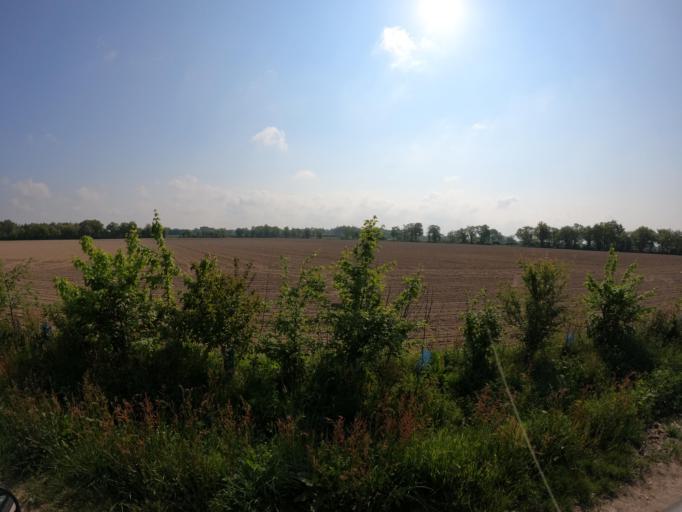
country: FR
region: Pays de la Loire
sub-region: Departement de la Vendee
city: Treize-Septiers
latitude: 47.0032
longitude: -1.2496
